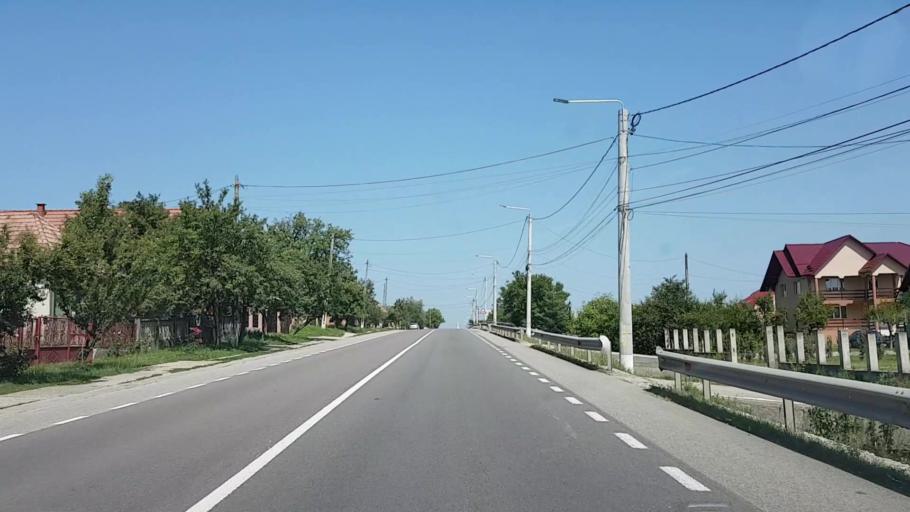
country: RO
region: Bistrita-Nasaud
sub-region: Comuna Ciceu-Mihaiesti
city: Ciceu-Mihaiesti
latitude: 47.1873
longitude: 23.9868
